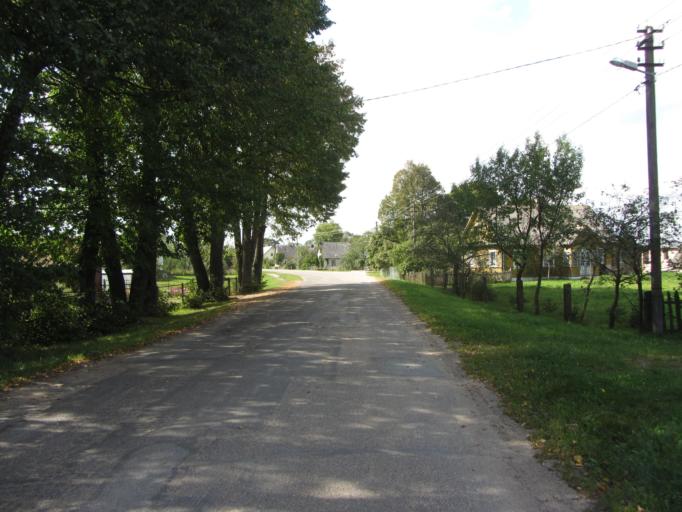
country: LT
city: Eisiskes
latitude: 54.1498
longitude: 25.0759
